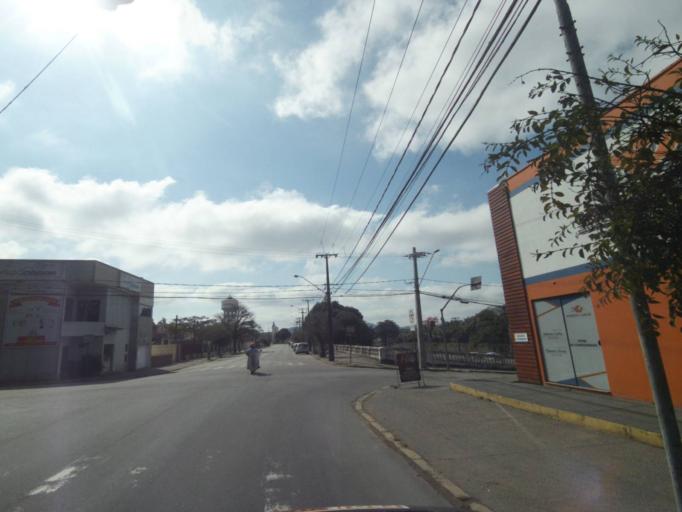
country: BR
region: Parana
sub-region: Paranagua
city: Paranagua
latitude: -25.5248
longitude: -48.5135
